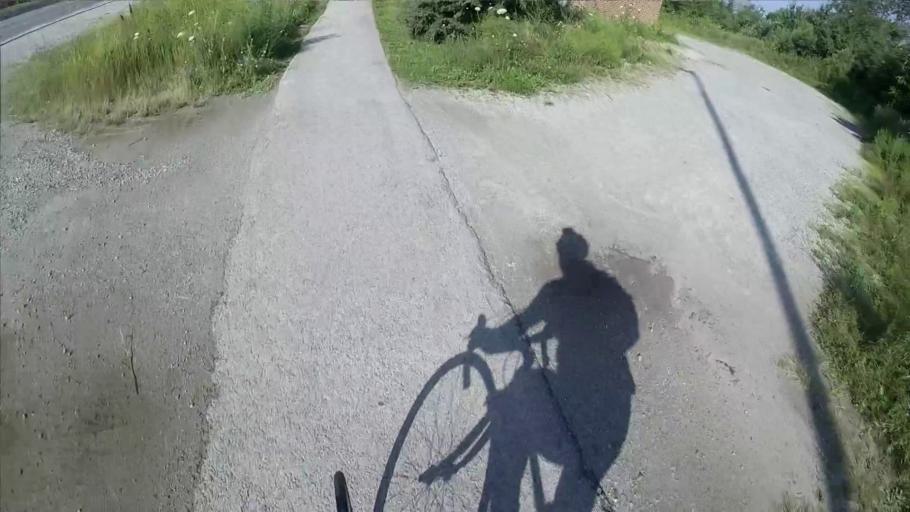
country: CA
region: Ontario
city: Burlington
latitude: 43.3968
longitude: -79.8189
